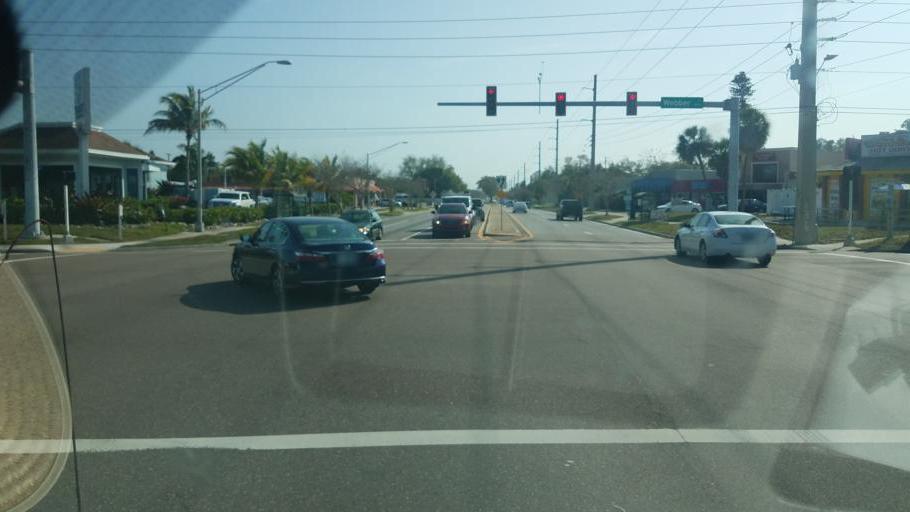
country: US
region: Florida
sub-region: Sarasota County
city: Southgate
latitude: 27.3085
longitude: -82.4976
